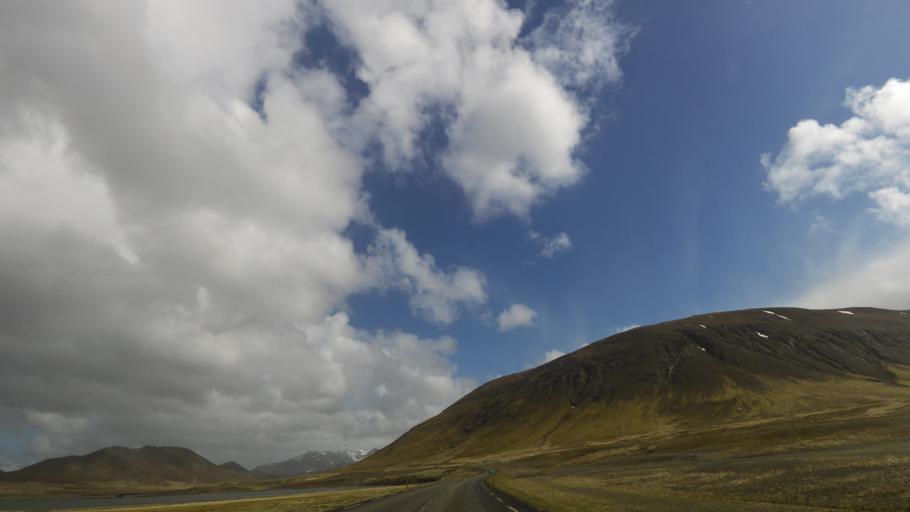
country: IS
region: West
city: Stykkisholmur
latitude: 64.9575
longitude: -23.0511
